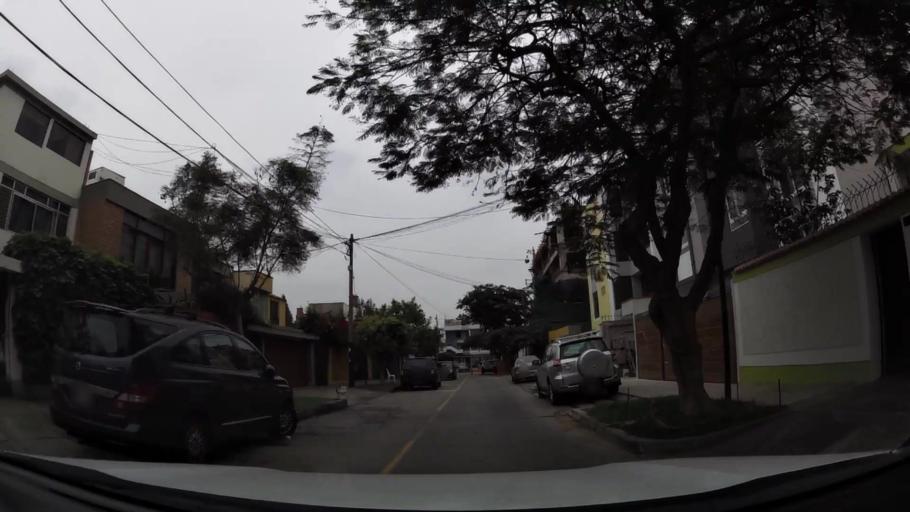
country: PE
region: Lima
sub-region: Lima
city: Surco
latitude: -12.1331
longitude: -77.0100
